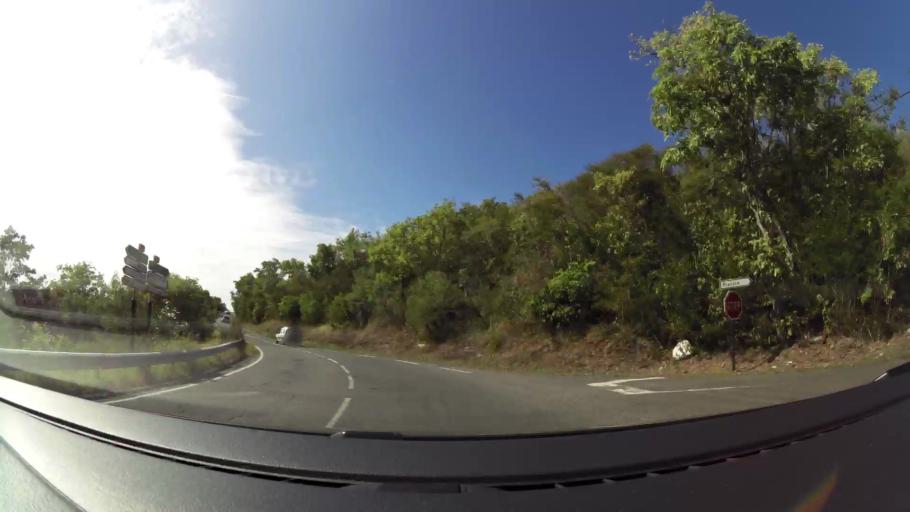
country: GP
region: Guadeloupe
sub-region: Guadeloupe
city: Vieux-Habitants
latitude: 16.0479
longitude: -61.7598
